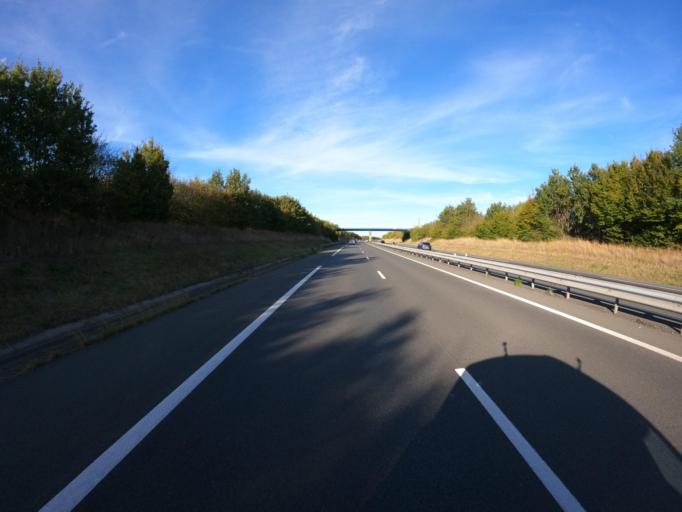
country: FR
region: Pays de la Loire
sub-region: Departement de Maine-et-Loire
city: Moze-sur-Louet
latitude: 47.3553
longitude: -0.5831
